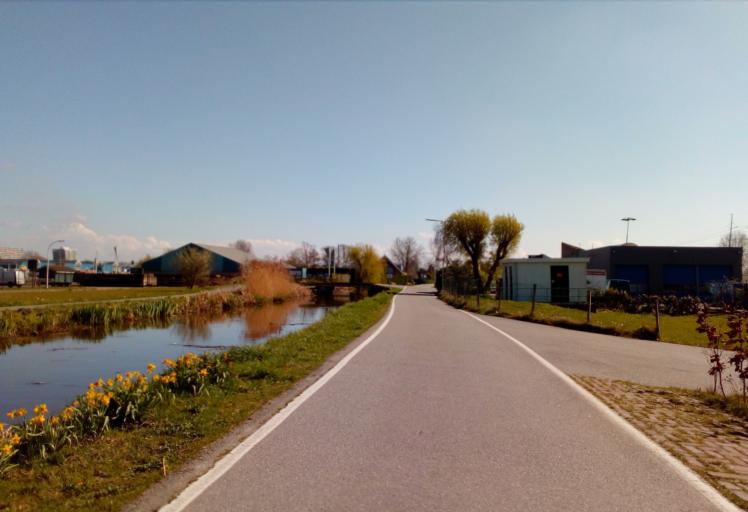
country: NL
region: South Holland
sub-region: Gemeente Delft
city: Delft
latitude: 51.9991
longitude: 4.3192
